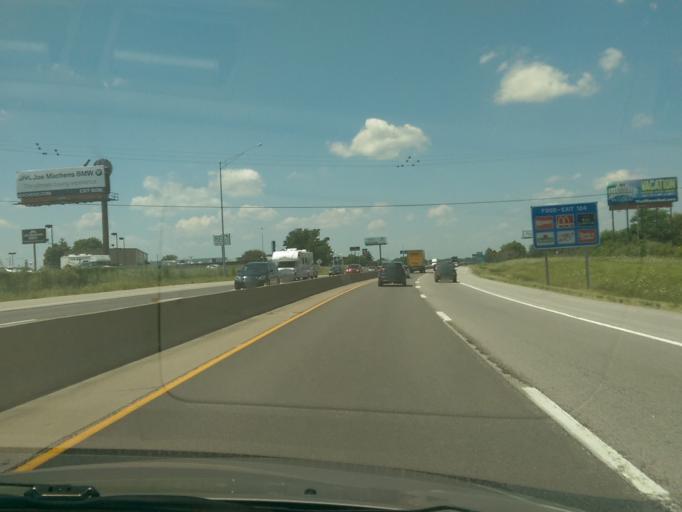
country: US
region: Missouri
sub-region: Boone County
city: Columbia
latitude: 38.9649
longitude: -92.3617
